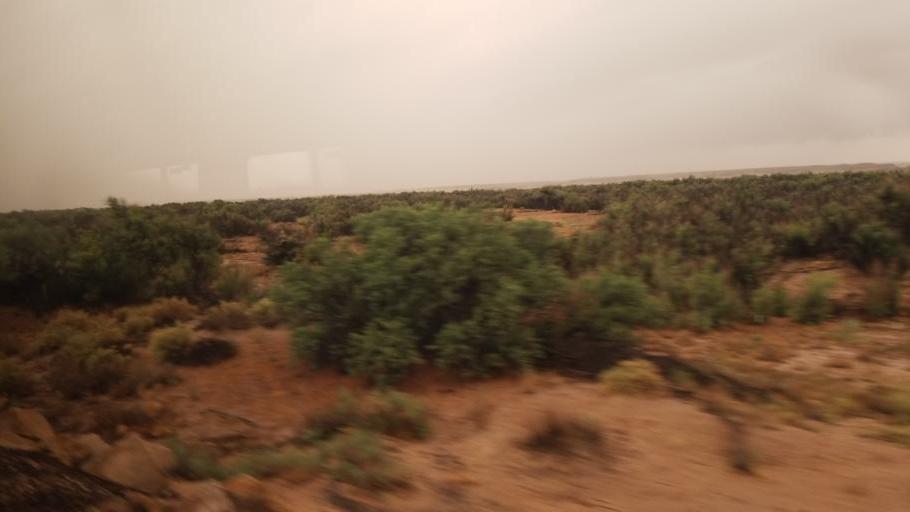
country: US
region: Arizona
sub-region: Navajo County
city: Joseph City
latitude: 34.9576
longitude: -110.3704
